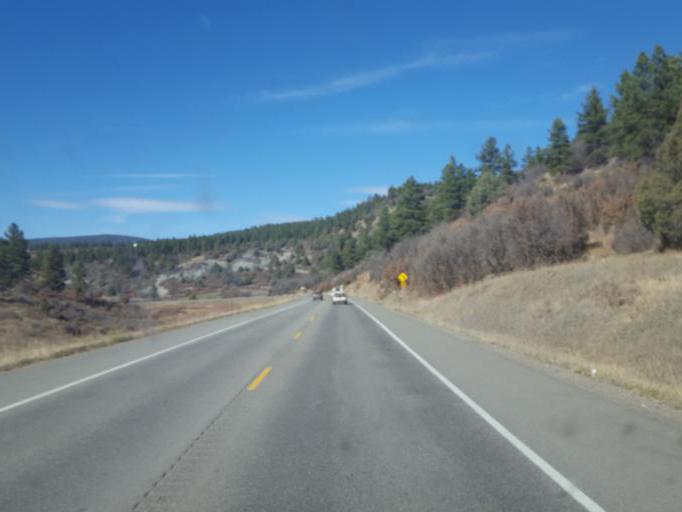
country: US
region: Colorado
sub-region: Archuleta County
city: Pagosa Springs
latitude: 37.2356
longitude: -107.1279
